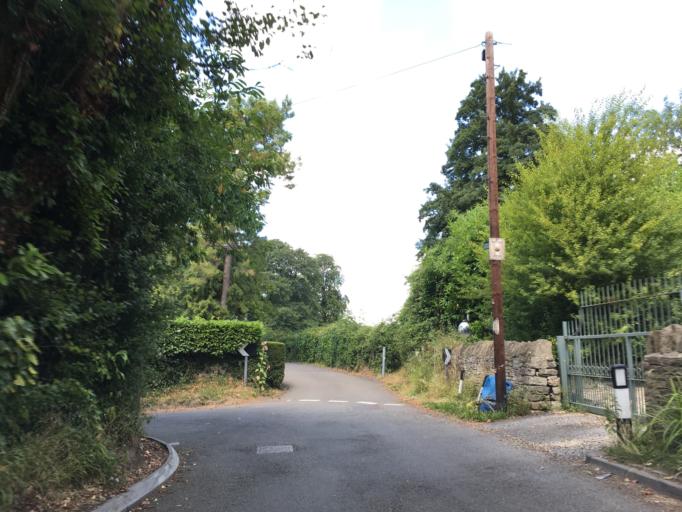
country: GB
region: England
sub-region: Gloucestershire
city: Barnwood
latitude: 51.8334
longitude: -2.1900
